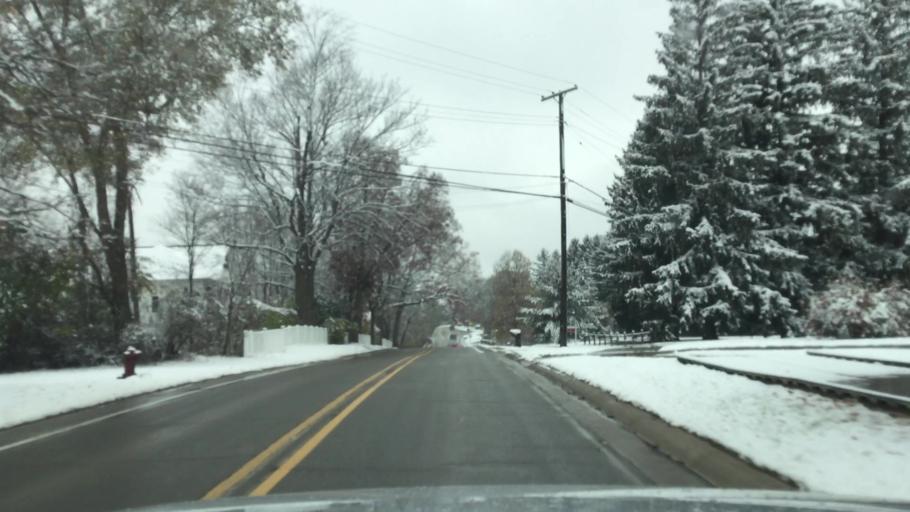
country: US
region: Michigan
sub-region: Oakland County
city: Oxford
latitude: 42.8096
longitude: -83.2816
